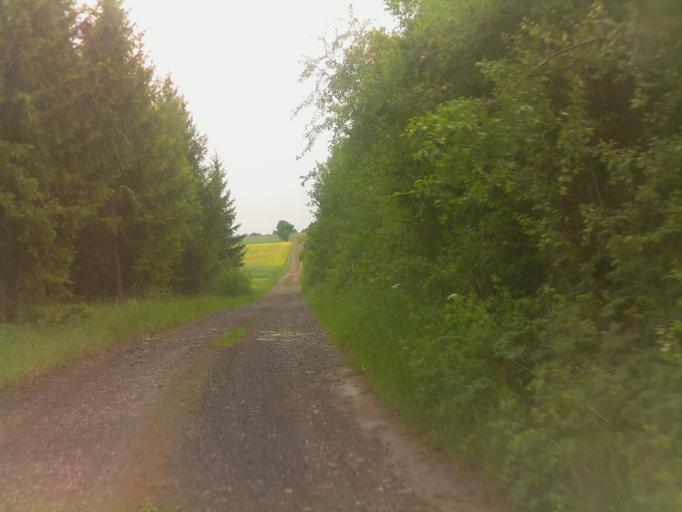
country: DE
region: Thuringia
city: Marisfeld
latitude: 50.5412
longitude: 10.5759
